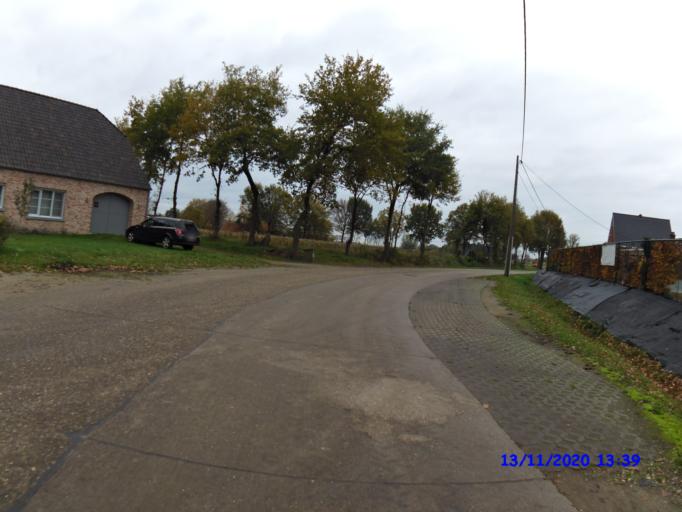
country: BE
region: Flanders
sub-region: Provincie Antwerpen
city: Kasterlee
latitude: 51.2493
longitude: 4.9910
